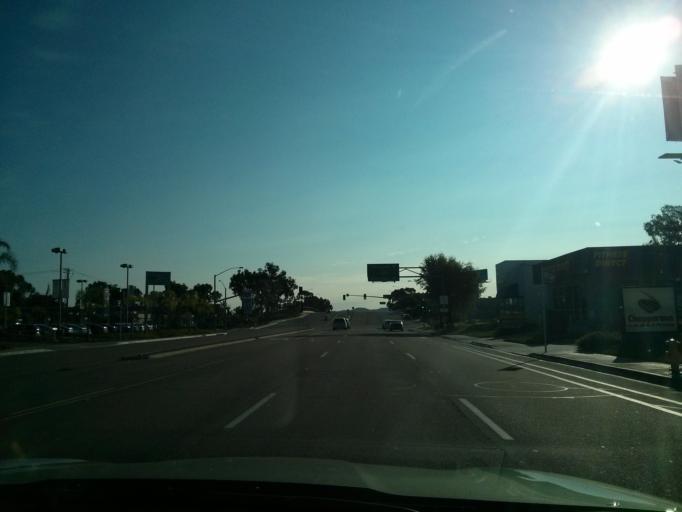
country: US
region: California
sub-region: San Diego County
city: San Diego
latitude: 32.8217
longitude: -117.1503
